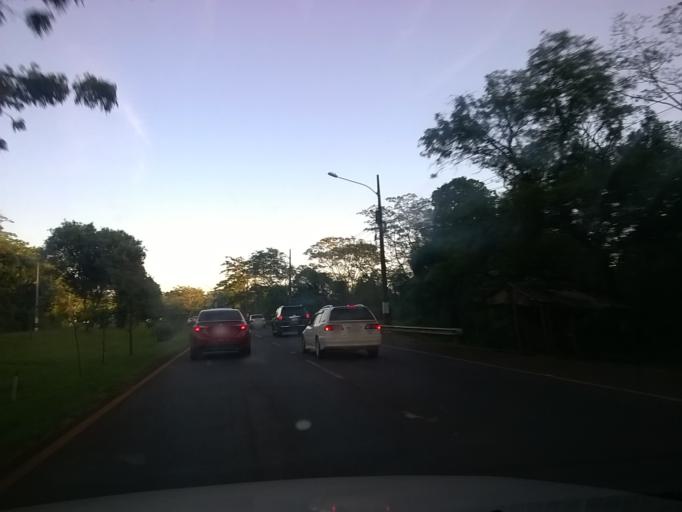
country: PY
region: Alto Parana
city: Ciudad del Este
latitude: -25.4558
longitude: -54.6259
